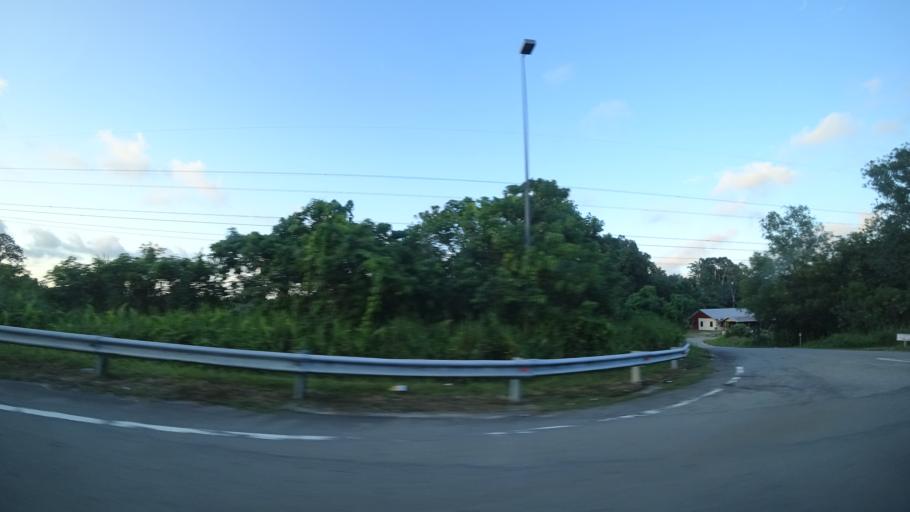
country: BN
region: Tutong
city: Tutong
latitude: 4.8307
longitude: 114.7280
